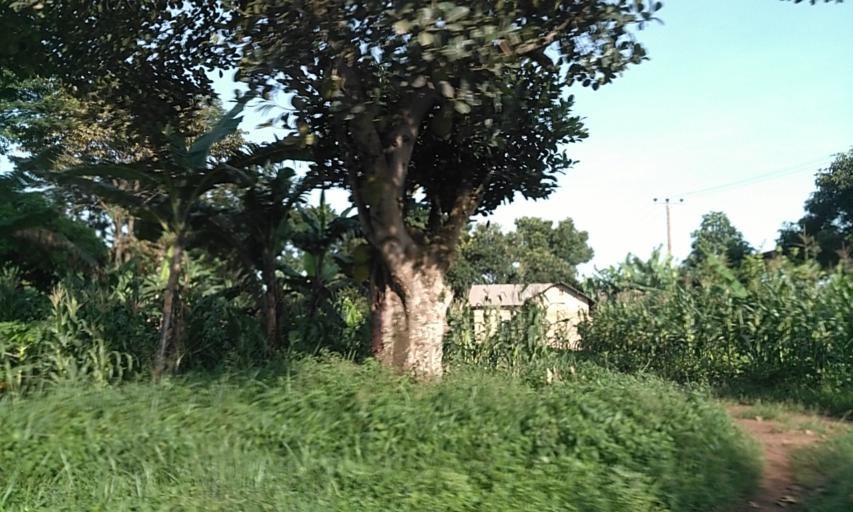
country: UG
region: Central Region
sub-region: Wakiso District
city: Bweyogerere
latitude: 0.4713
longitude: 32.6608
